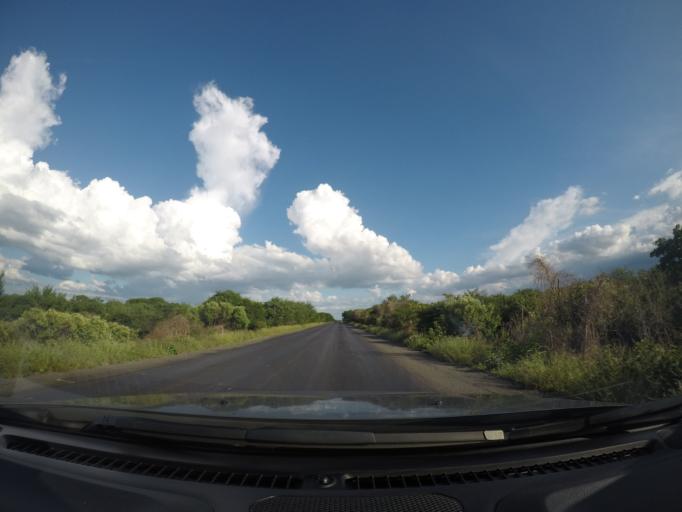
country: BR
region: Bahia
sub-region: Oliveira Dos Brejinhos
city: Oliveira dos Brejinhos
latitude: -12.0882
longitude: -42.9338
